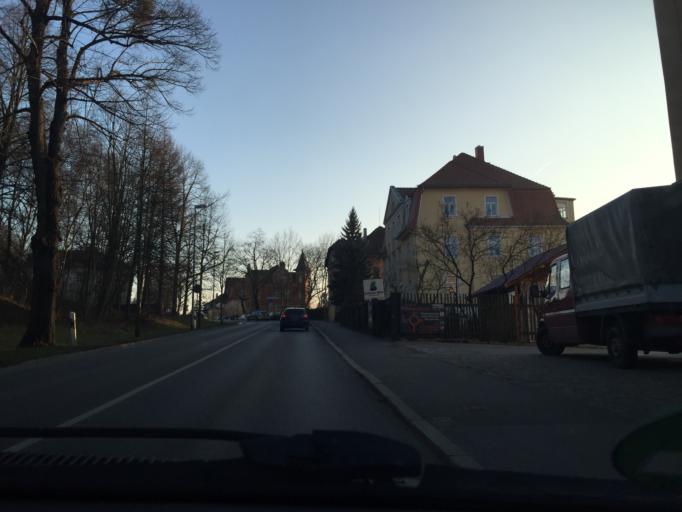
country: DE
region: Saxony
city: Pirna
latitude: 50.9569
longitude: 13.9447
